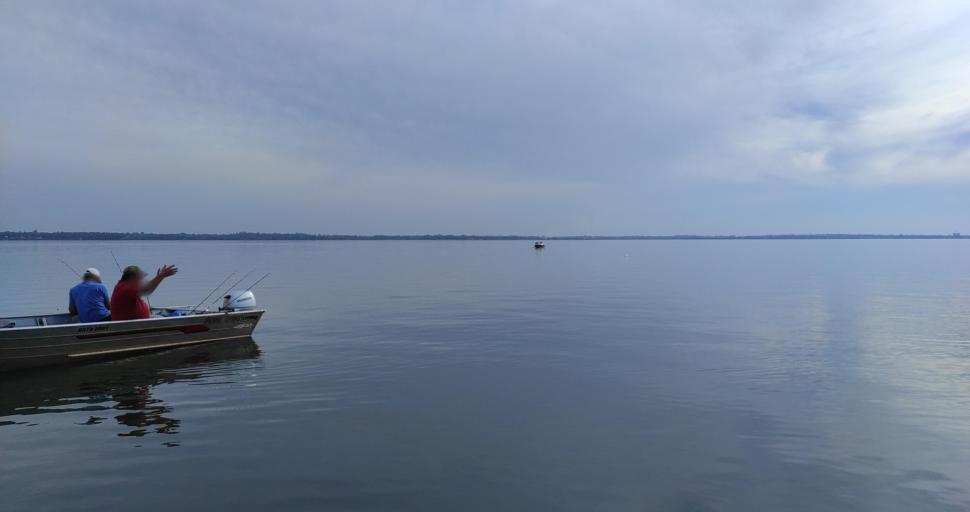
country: AR
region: Misiones
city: Garupa
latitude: -27.4222
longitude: -55.8226
